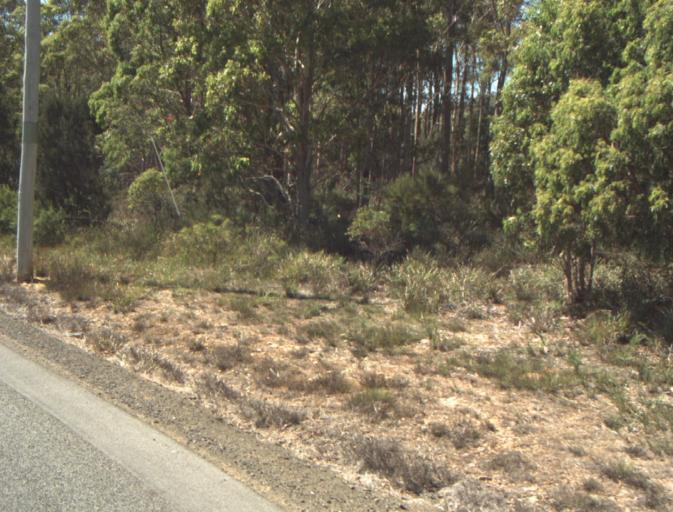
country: AU
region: Tasmania
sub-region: Launceston
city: Newstead
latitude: -41.3188
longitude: 147.3266
